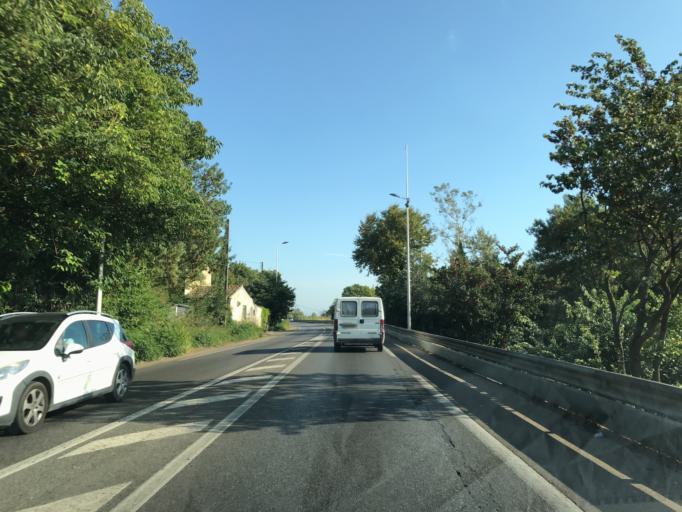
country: FR
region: Provence-Alpes-Cote d'Azur
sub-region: Departement des Bouches-du-Rhone
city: Saint-Chamas
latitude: 43.5566
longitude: 5.0323
